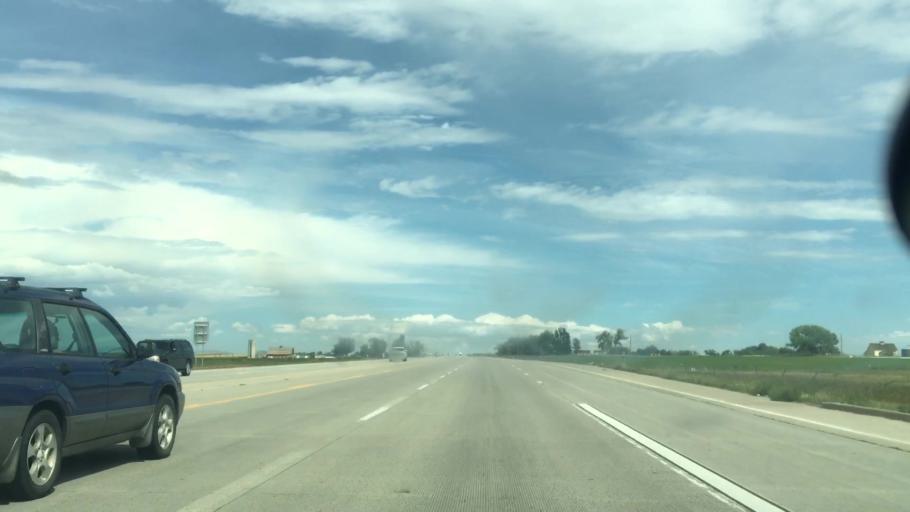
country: US
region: Colorado
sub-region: Boulder County
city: Longmont
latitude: 40.2089
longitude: -105.1023
